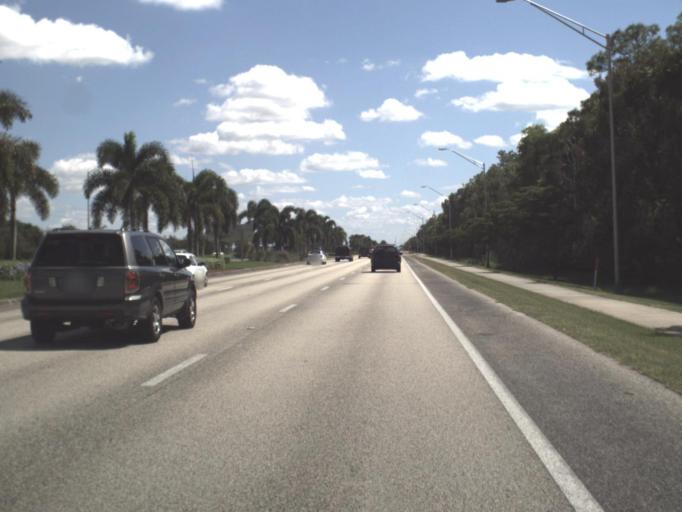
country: US
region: Florida
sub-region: Collier County
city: Lely Resort
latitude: 26.0728
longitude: -81.7143
